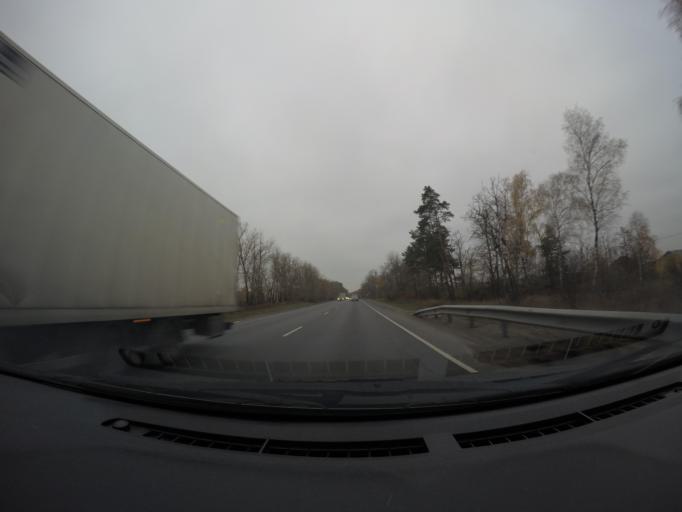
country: RU
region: Moskovskaya
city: Malyshevo
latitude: 55.4561
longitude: 38.3286
